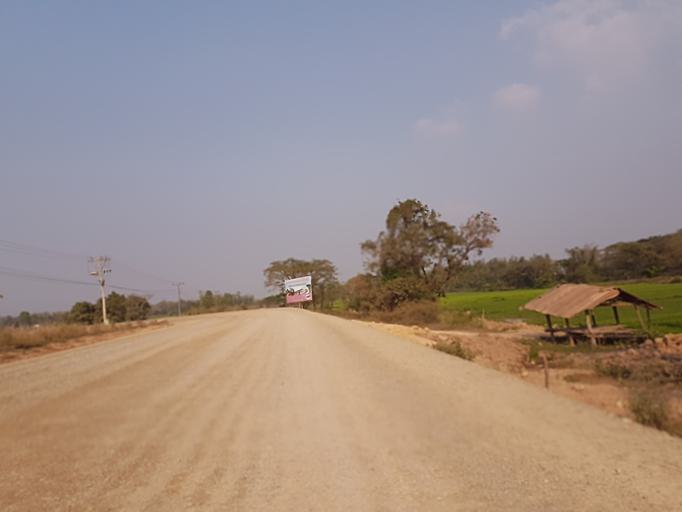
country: TH
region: Nong Khai
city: Phon Phisai
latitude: 17.9928
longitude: 102.9083
